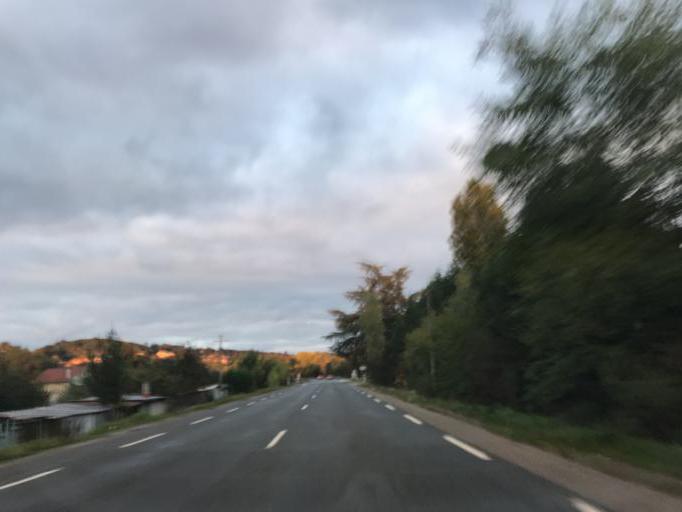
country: FR
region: Rhone-Alpes
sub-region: Departement de l'Ain
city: Trevoux
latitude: 45.9352
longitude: 4.7727
